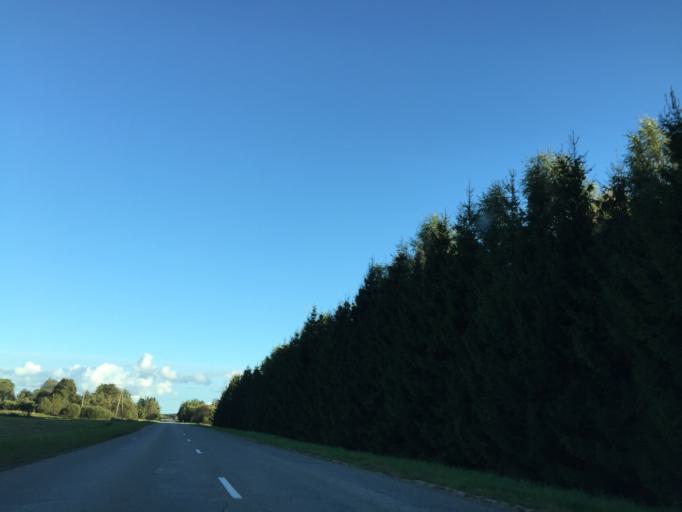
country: LV
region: Kuldigas Rajons
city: Kuldiga
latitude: 56.9455
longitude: 22.0187
